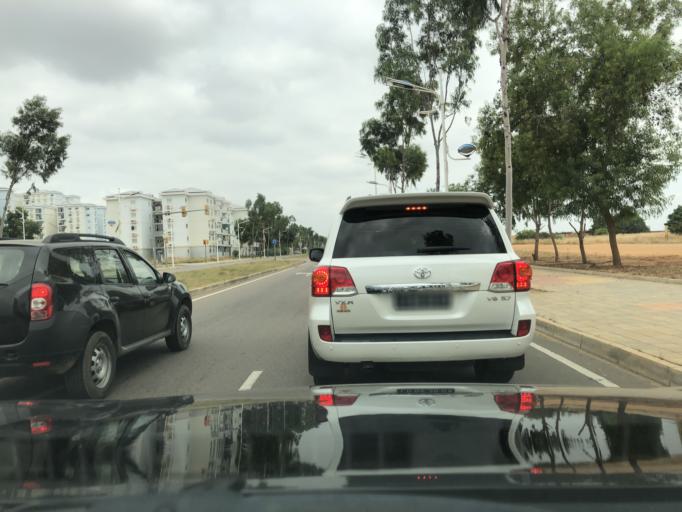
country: AO
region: Luanda
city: Luanda
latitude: -8.9911
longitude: 13.2779
